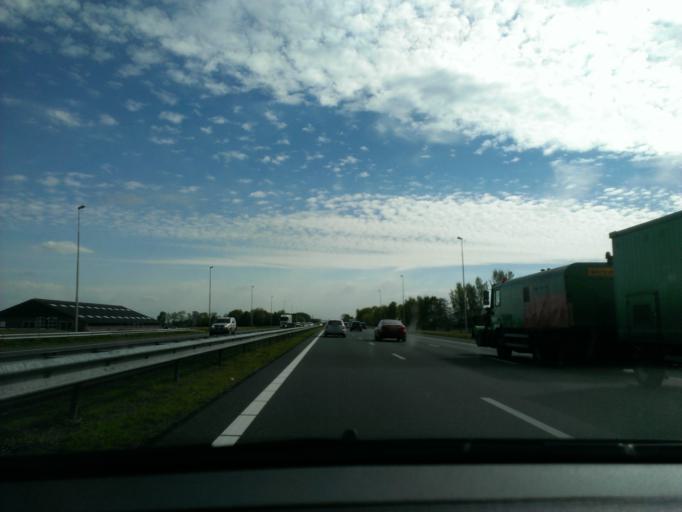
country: NL
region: Overijssel
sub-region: Gemeente Staphorst
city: Staphorst
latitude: 52.5659
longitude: 6.1818
